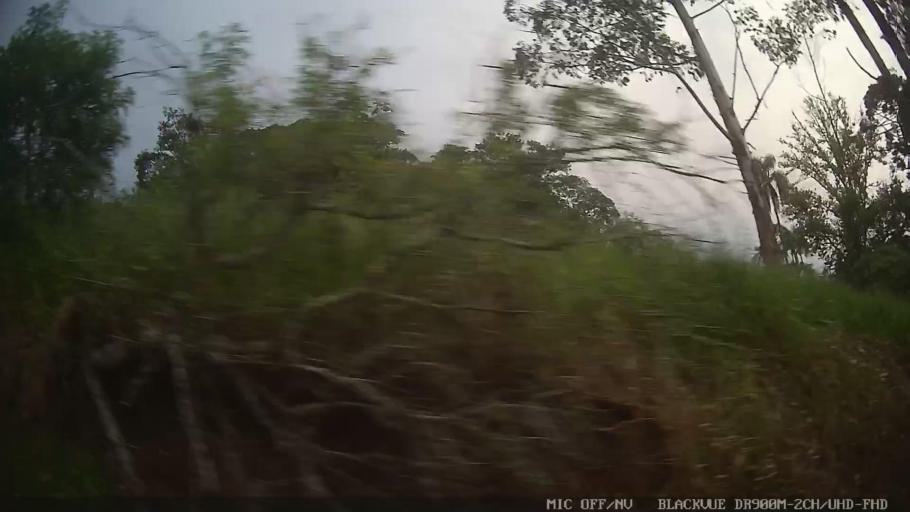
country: BR
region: Sao Paulo
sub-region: Ribeirao Pires
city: Ribeirao Pires
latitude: -23.6779
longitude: -46.3164
